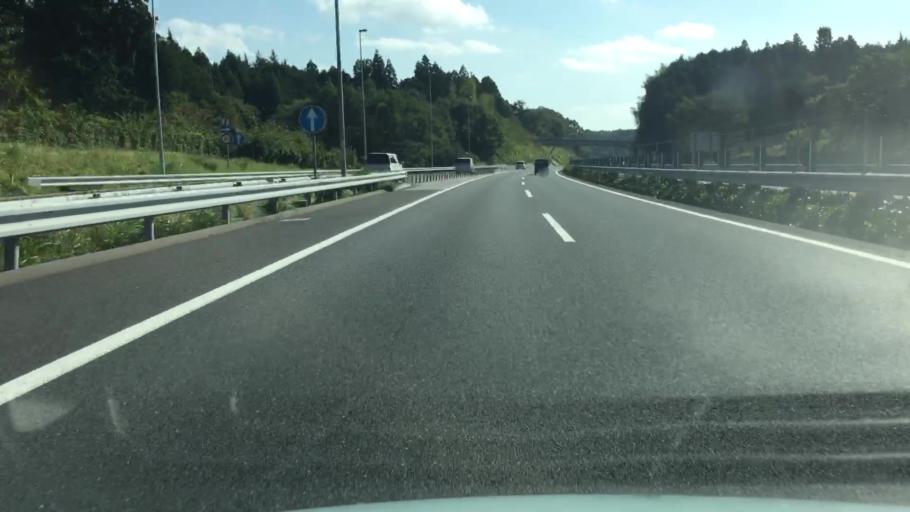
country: JP
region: Ibaraki
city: Kasama
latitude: 36.3437
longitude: 140.2568
